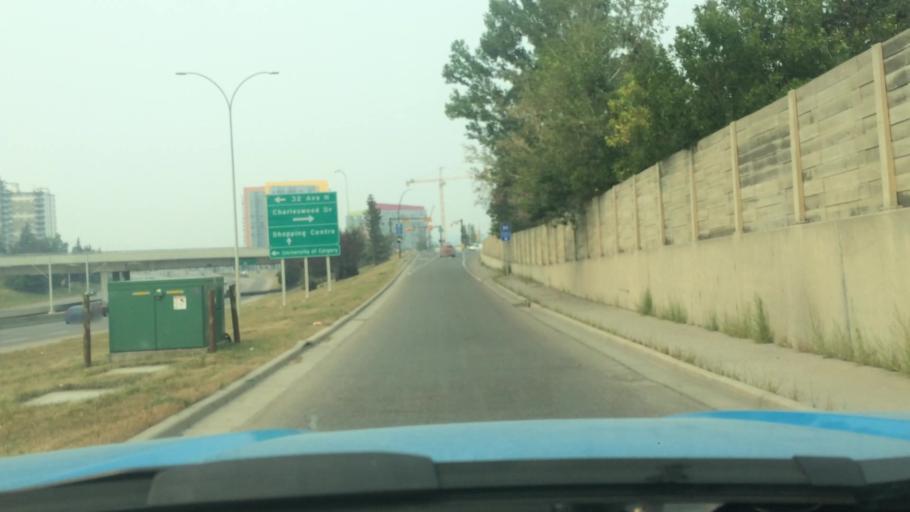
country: CA
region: Alberta
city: Calgary
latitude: 51.0820
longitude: -114.1240
